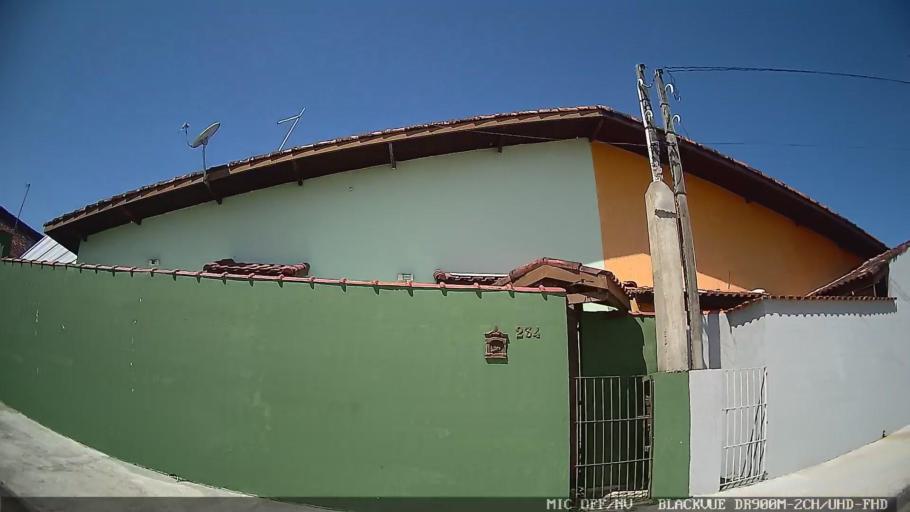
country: BR
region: Sao Paulo
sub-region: Peruibe
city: Peruibe
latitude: -24.3079
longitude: -46.9984
